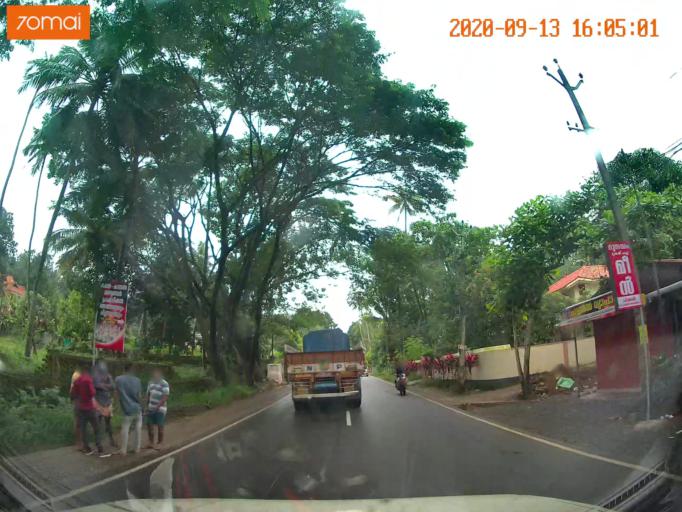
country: IN
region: Kerala
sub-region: Kottayam
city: Palackattumala
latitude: 9.6694
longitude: 76.5732
